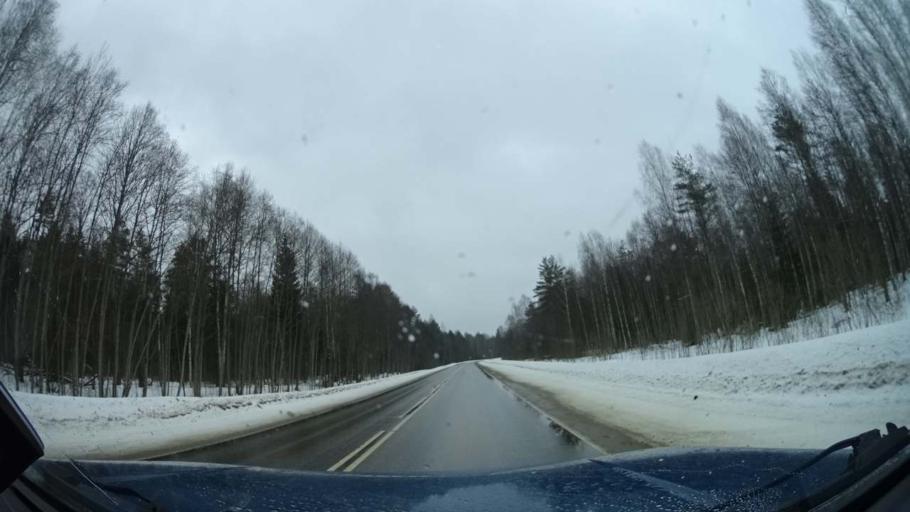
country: RU
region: Tverskaya
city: Radchenko
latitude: 56.8578
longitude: 36.4496
